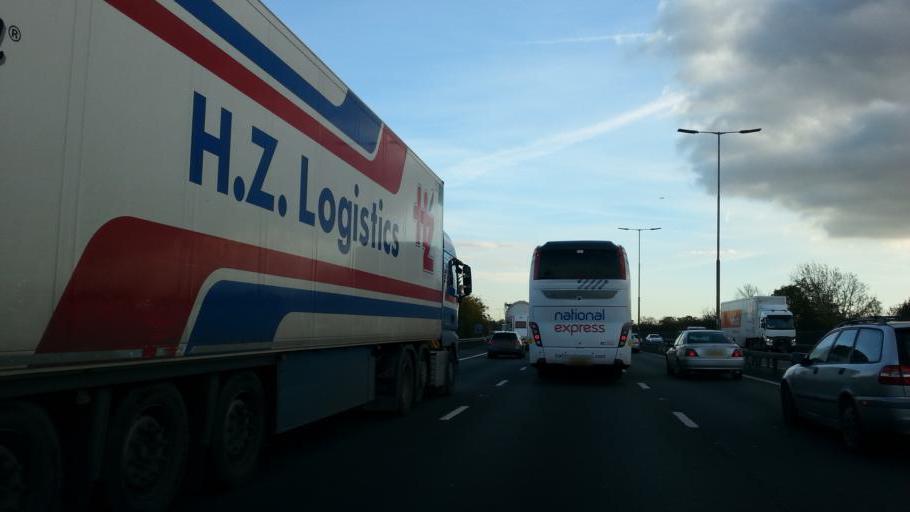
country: GB
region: England
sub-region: Royal Borough of Windsor and Maidenhead
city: Datchet
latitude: 51.4918
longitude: -0.5815
